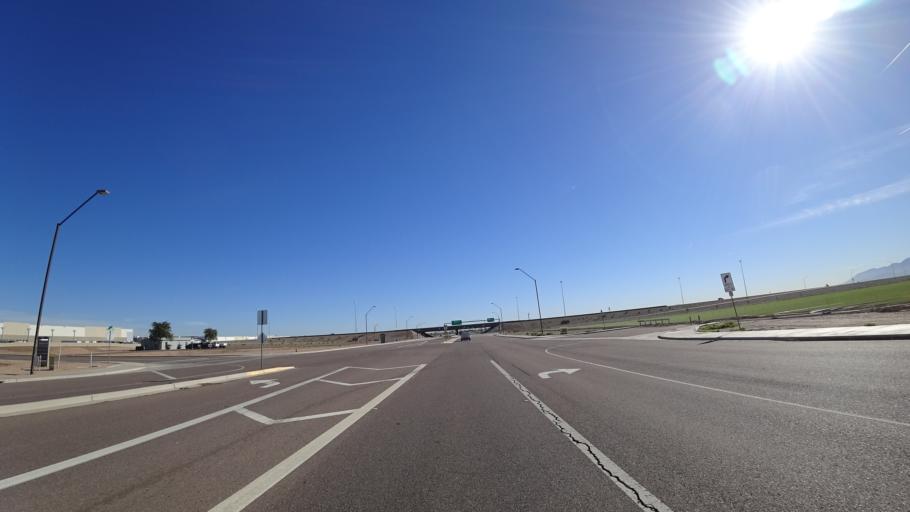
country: US
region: Arizona
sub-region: Maricopa County
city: Citrus Park
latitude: 33.4937
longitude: -112.4242
